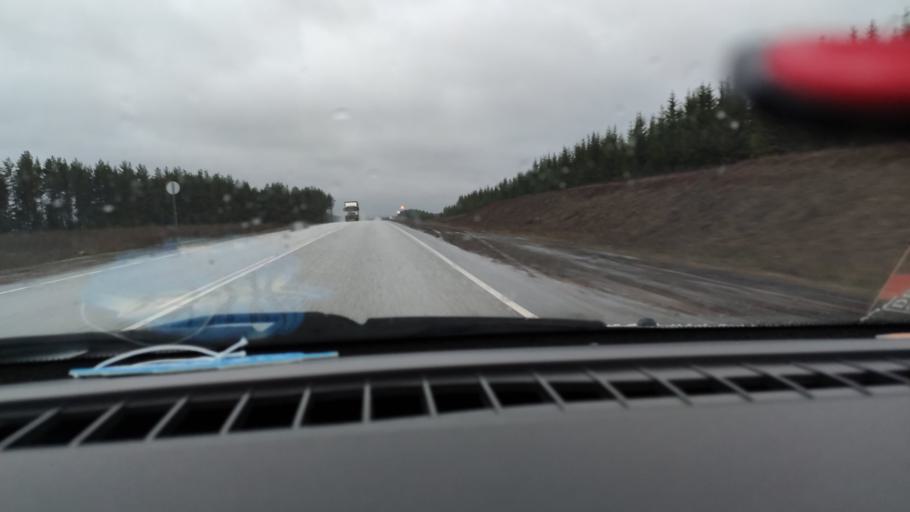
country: RU
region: Udmurtiya
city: Alnashi
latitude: 56.0524
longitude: 52.3919
